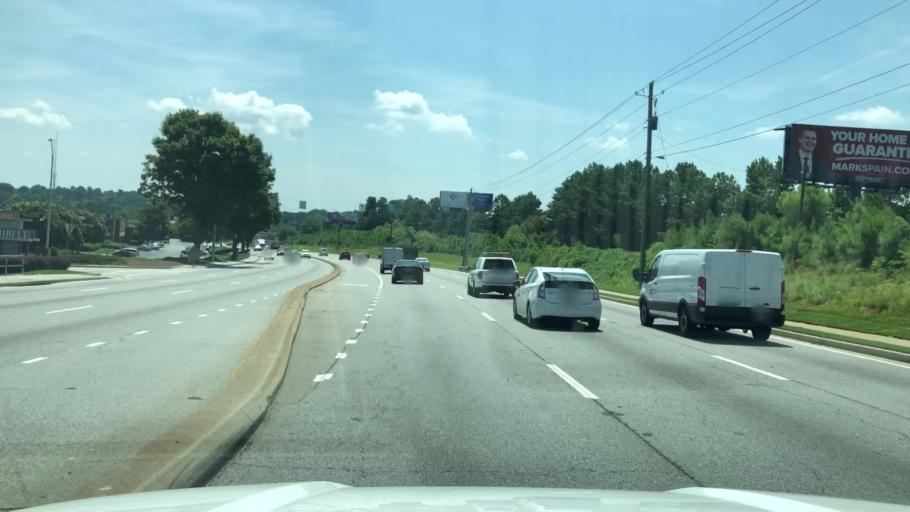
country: US
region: Georgia
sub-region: Gwinnett County
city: Norcross
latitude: 33.9274
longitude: -84.2196
